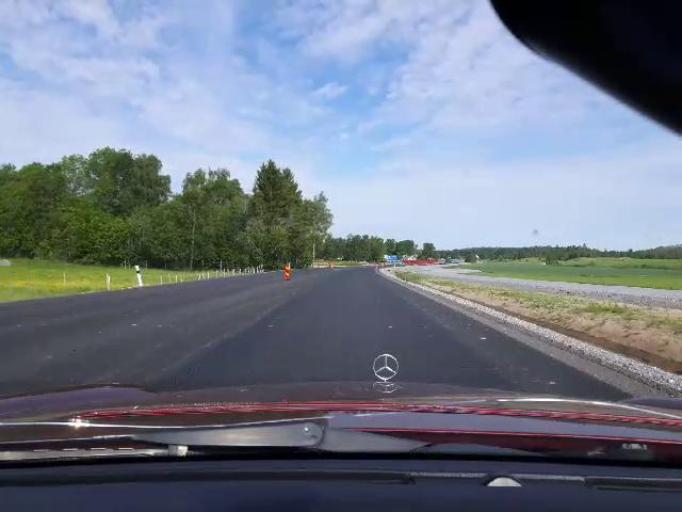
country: SE
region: Uppsala
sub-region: Enkopings Kommun
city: Irsta
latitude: 59.7628
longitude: 16.9195
